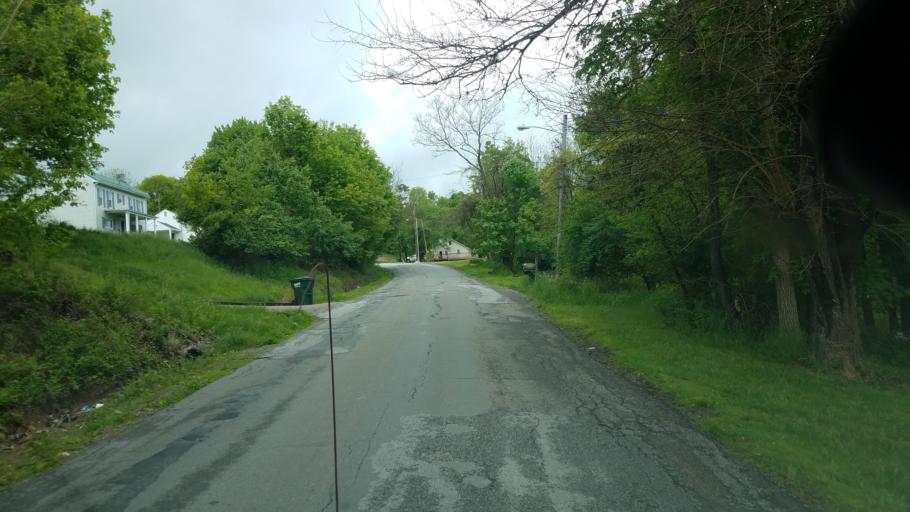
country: US
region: Ohio
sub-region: Harrison County
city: Cadiz
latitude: 40.2714
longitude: -80.9830
